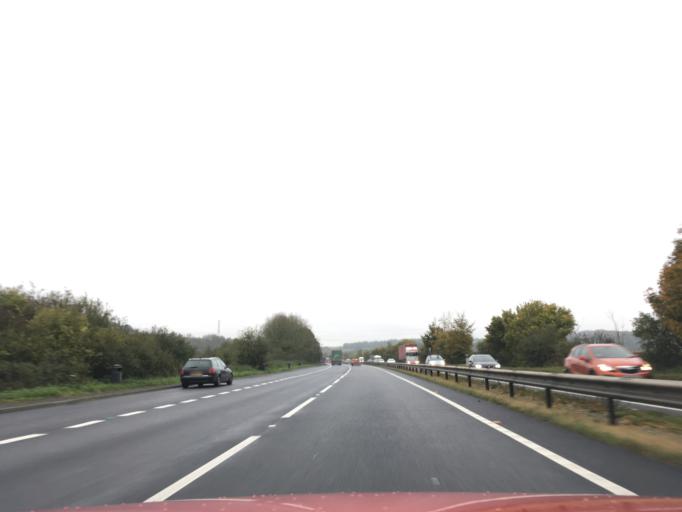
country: GB
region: England
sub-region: Hampshire
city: Highclere
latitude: 51.3037
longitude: -1.3360
